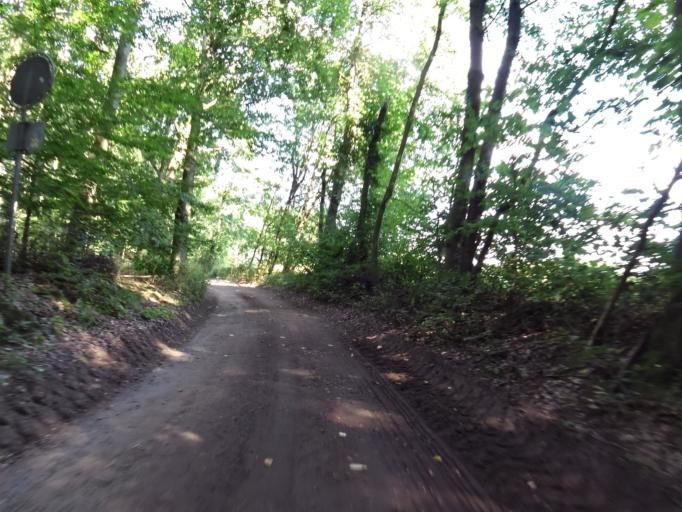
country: DE
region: Rheinland-Pfalz
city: Wattenheim
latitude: 49.5230
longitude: 8.0444
